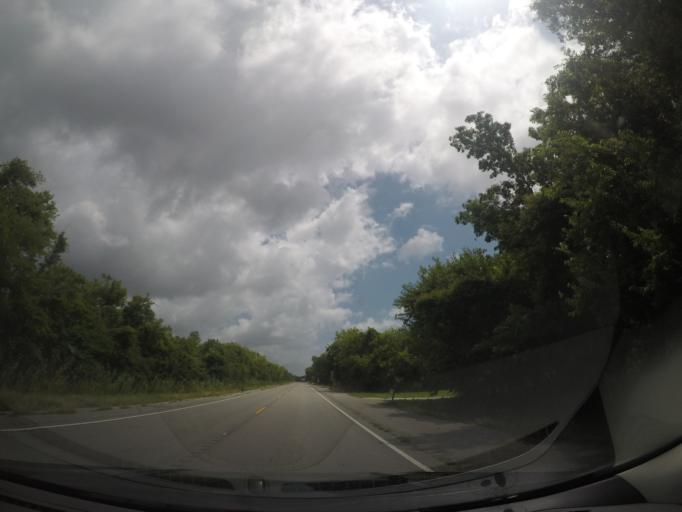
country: US
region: Louisiana
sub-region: Saint Tammany Parish
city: Eden Isle
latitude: 30.1007
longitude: -89.7647
